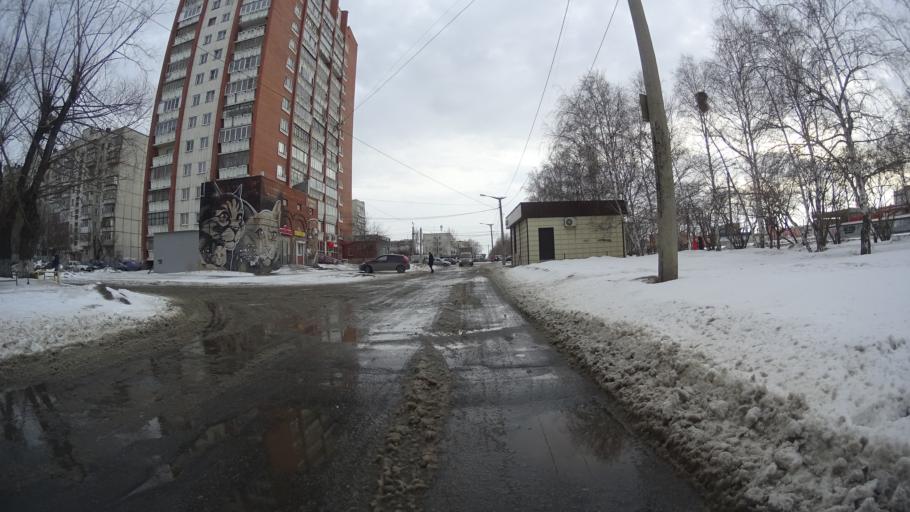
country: RU
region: Chelyabinsk
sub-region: Gorod Chelyabinsk
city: Chelyabinsk
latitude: 55.1954
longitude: 61.3221
